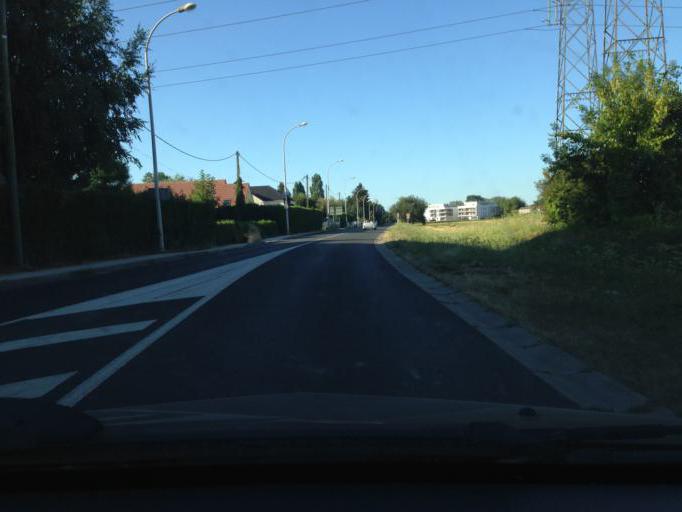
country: FR
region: Ile-de-France
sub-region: Departement des Yvelines
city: Saint-Remy-les-Chevreuse
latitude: 48.7163
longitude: 2.0861
